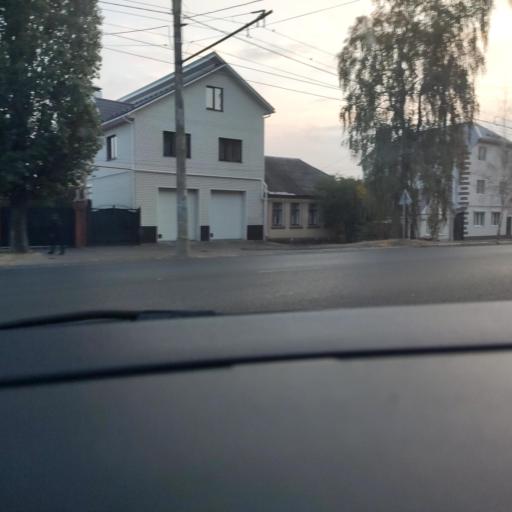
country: RU
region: Voronezj
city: Voronezh
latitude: 51.6987
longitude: 39.1913
